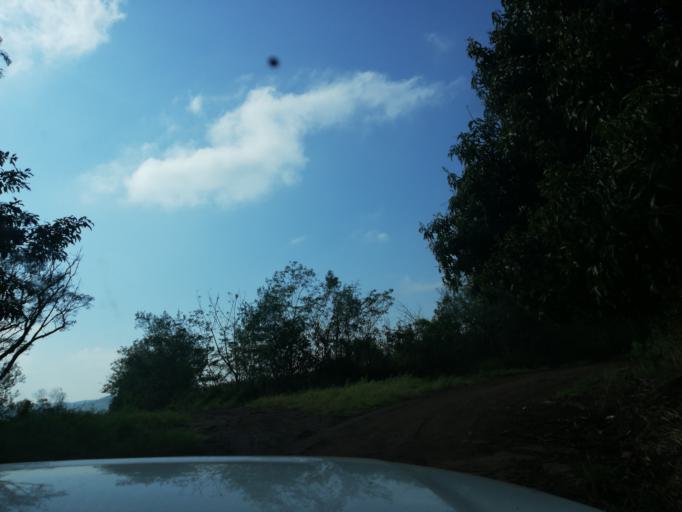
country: AR
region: Misiones
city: Cerro Azul
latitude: -27.6148
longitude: -55.5232
